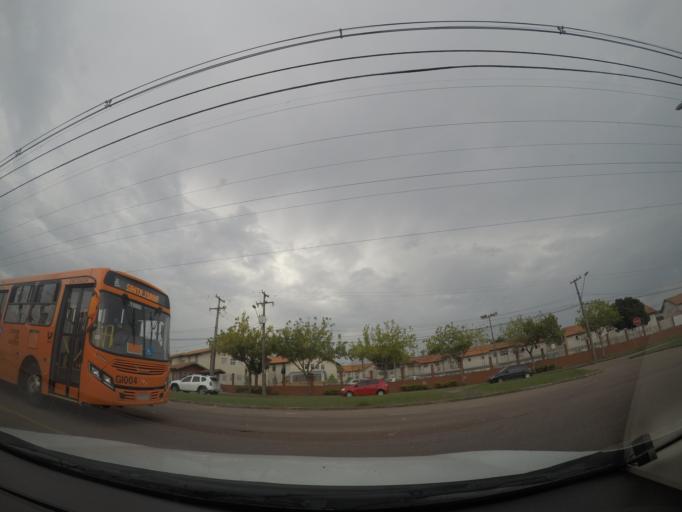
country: BR
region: Parana
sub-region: Sao Jose Dos Pinhais
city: Sao Jose dos Pinhais
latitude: -25.5388
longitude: -49.2763
